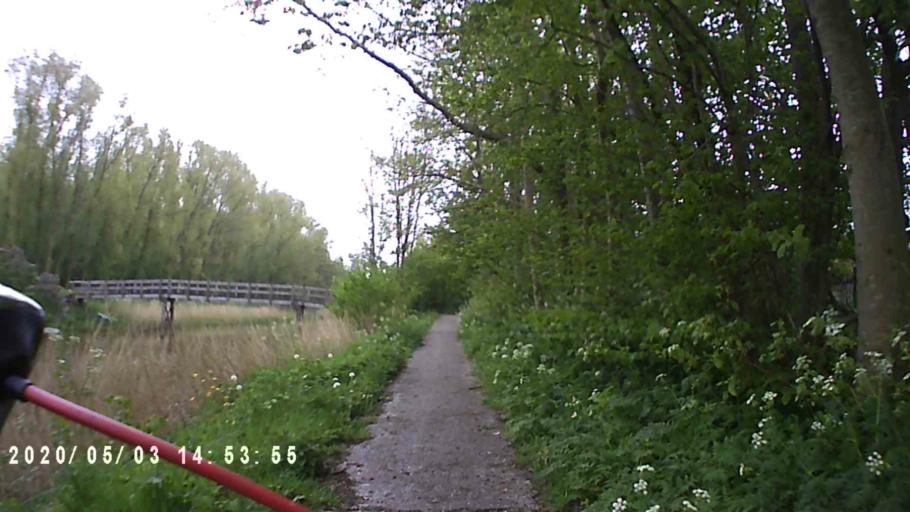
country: NL
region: Groningen
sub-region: Gemeente Zuidhorn
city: Oldehove
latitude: 53.3604
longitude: 6.4259
